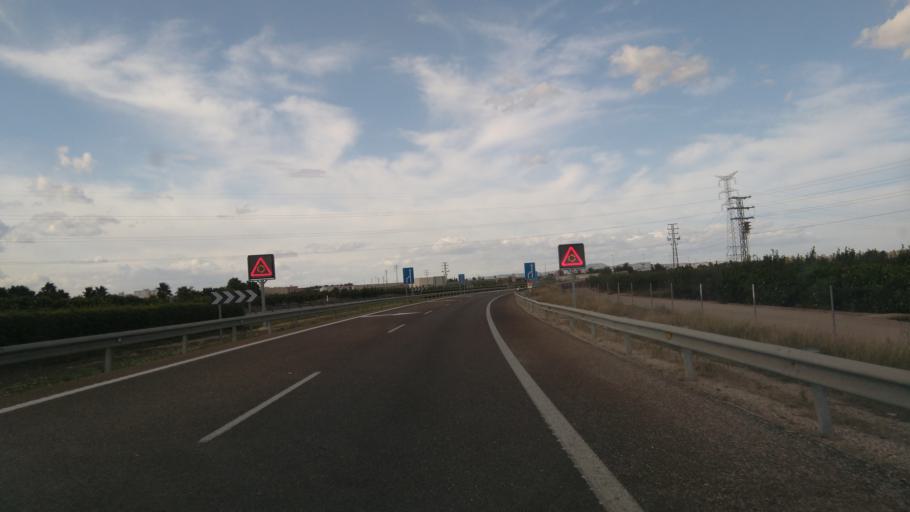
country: ES
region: Valencia
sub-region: Provincia de Valencia
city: L'Alcudia
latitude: 39.1877
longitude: -0.4922
